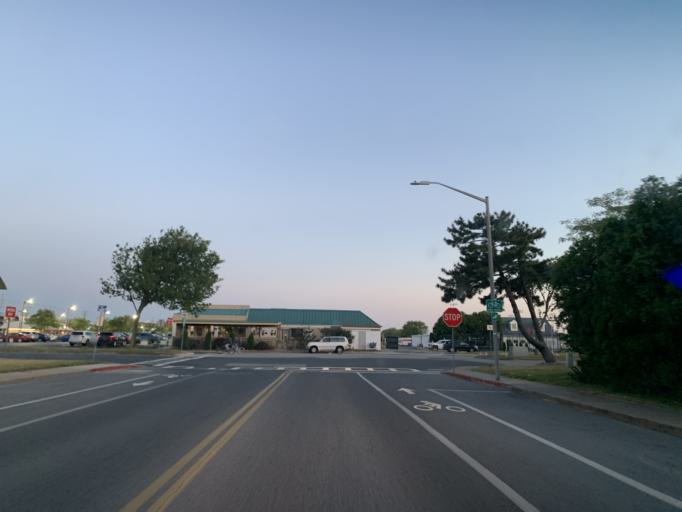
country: US
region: Delaware
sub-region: Sussex County
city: Bethany Beach
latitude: 38.4360
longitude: -75.0558
